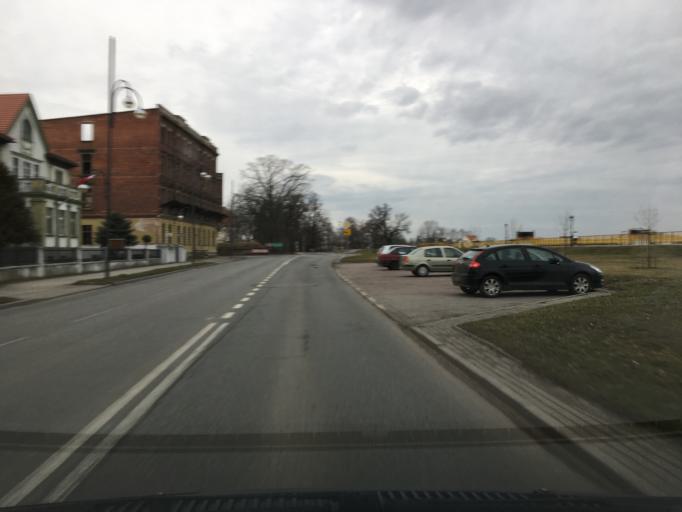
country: PL
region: Opole Voivodeship
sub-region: Powiat kedzierzynsko-kozielski
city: Kozle
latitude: 50.3365
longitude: 18.1460
